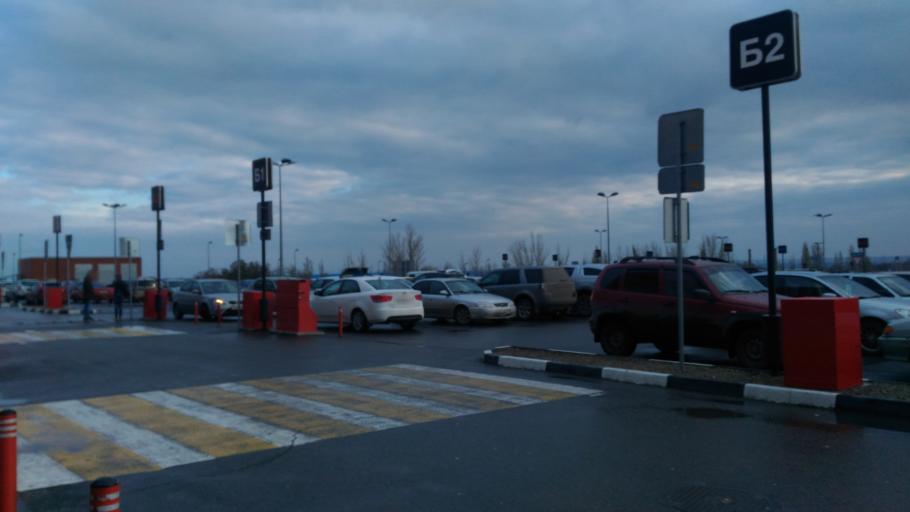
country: RU
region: Volgograd
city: Volgograd
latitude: 48.6352
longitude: 44.4353
